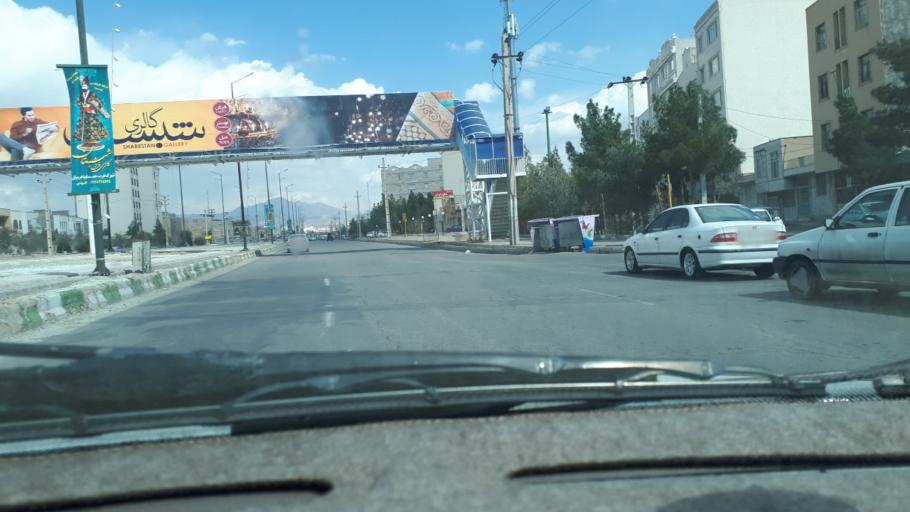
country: IR
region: Semnan
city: Semnan
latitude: 35.5843
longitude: 53.3769
